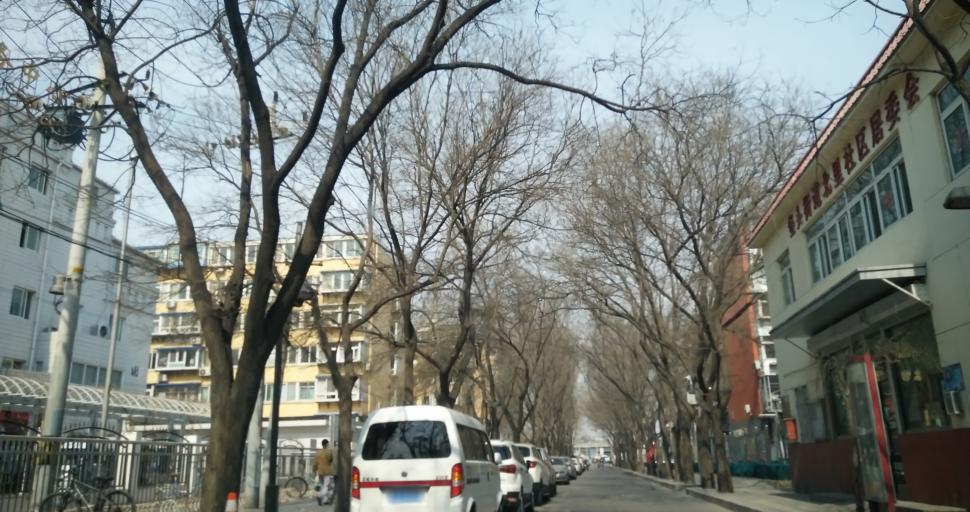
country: CN
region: Beijing
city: Dongfeng
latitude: 39.8666
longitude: 116.5043
